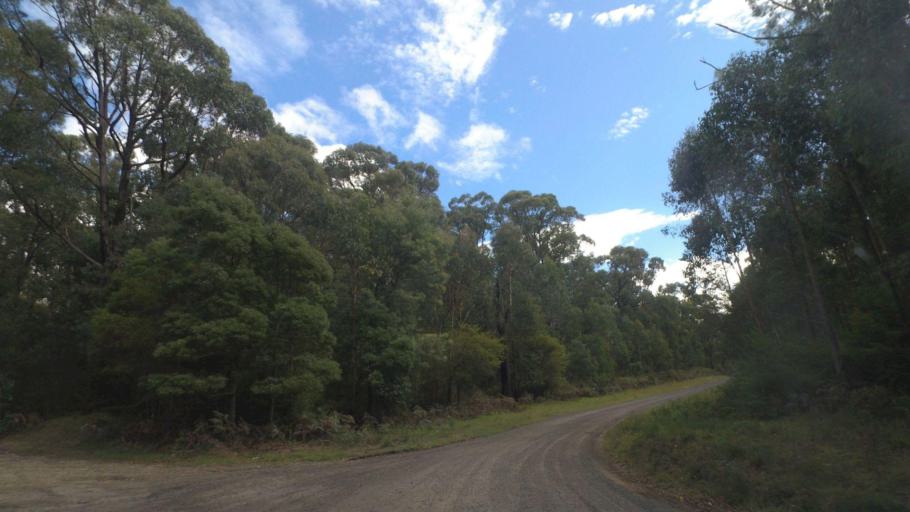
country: AU
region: Victoria
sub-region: Cardinia
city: Bunyip
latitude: -37.9903
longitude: 145.8112
